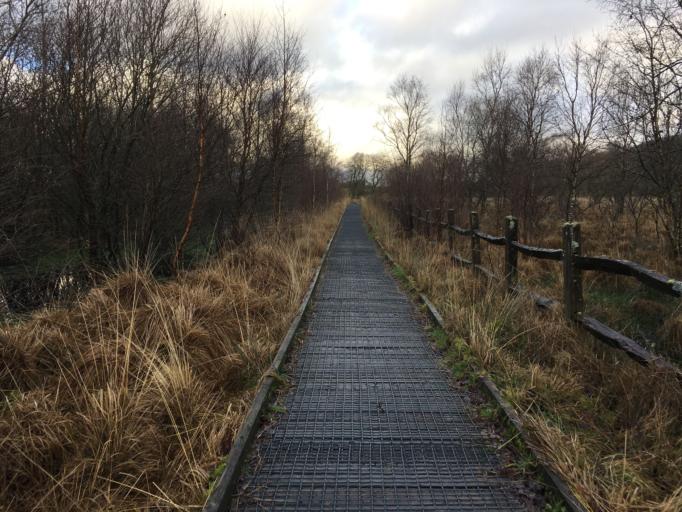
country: GB
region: Wales
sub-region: County of Ceredigion
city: Lledrod
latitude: 52.2435
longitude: -3.9217
